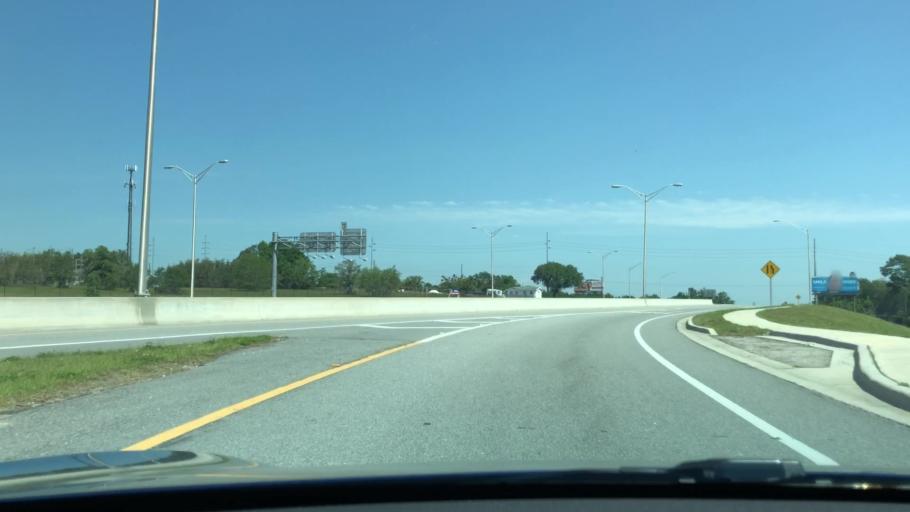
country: US
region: Florida
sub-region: Lake County
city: Minneola
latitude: 28.5489
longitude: -81.7417
